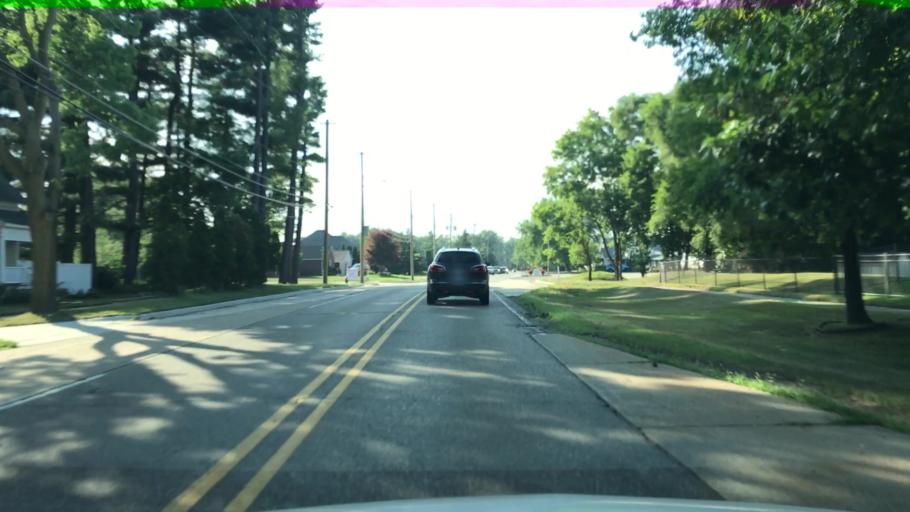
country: US
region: Michigan
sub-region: Macomb County
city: Fraser
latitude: 42.5830
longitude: -82.9756
